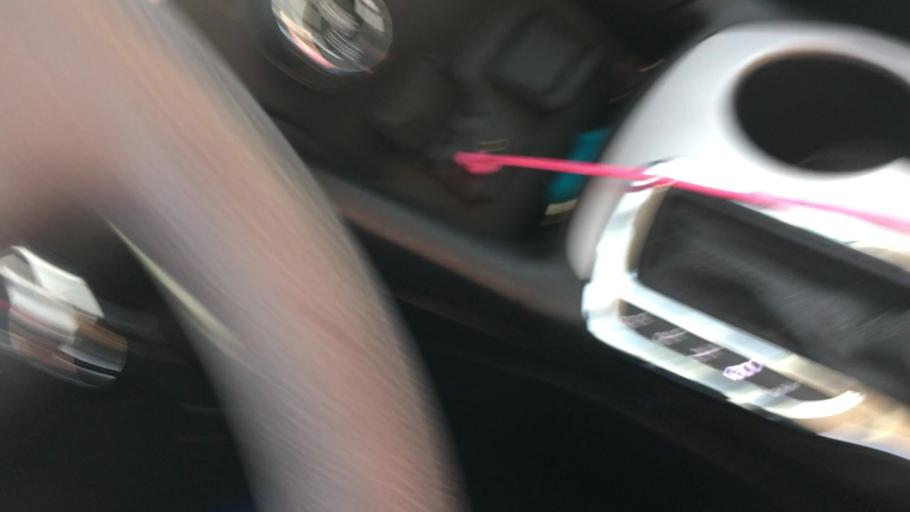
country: US
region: Florida
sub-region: Palm Beach County
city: Schall Circle
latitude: 26.7087
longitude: -80.1020
